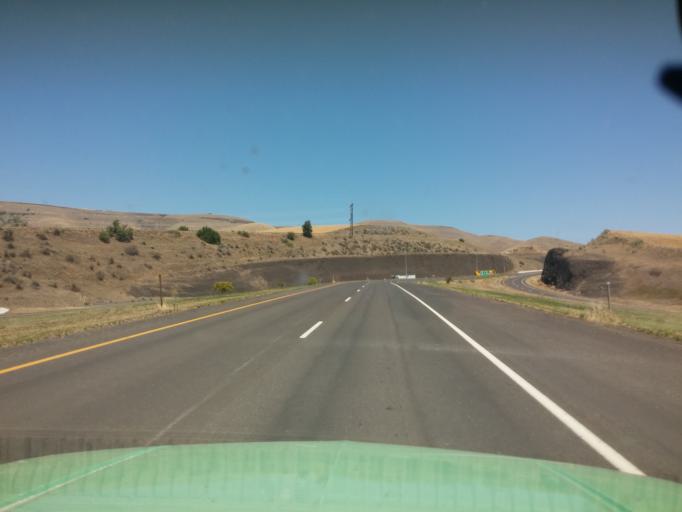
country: US
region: Idaho
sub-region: Nez Perce County
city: Lewiston
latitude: 46.4317
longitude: -116.9938
